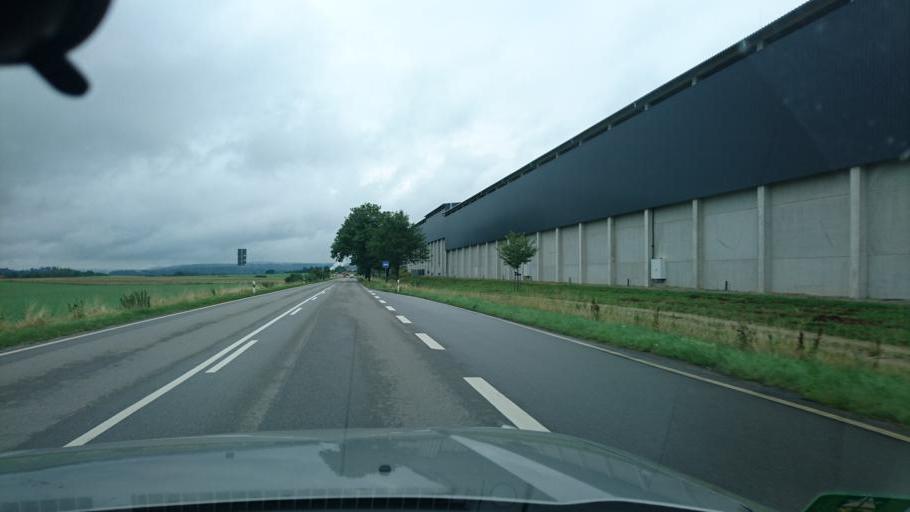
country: DE
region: Baden-Wuerttemberg
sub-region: Freiburg Region
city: Deisslingen
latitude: 48.1143
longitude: 8.6164
